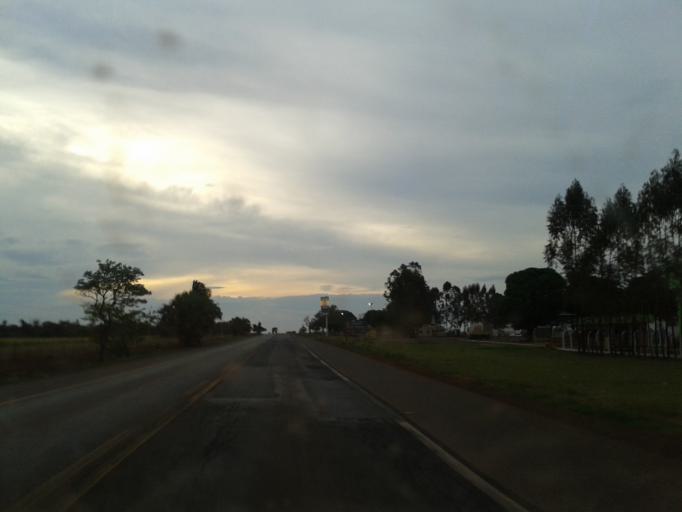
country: BR
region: Goias
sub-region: Santa Helena De Goias
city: Santa Helena de Goias
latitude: -17.9360
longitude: -50.5389
